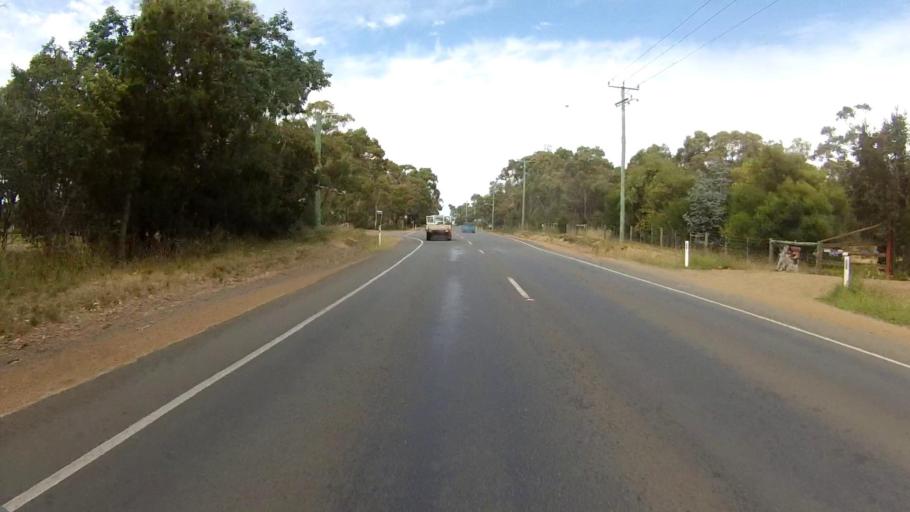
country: AU
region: Tasmania
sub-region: Clarence
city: Sandford
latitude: -42.9431
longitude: 147.4984
